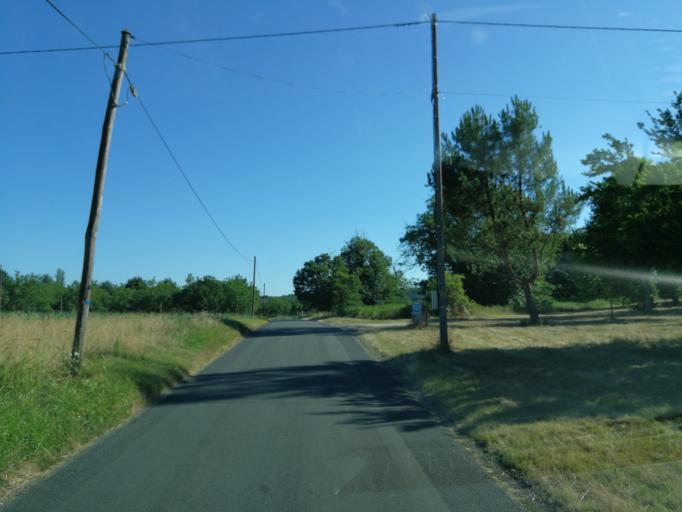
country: FR
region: Midi-Pyrenees
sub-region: Departement du Lot
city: Gourdon
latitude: 44.8305
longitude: 1.3608
